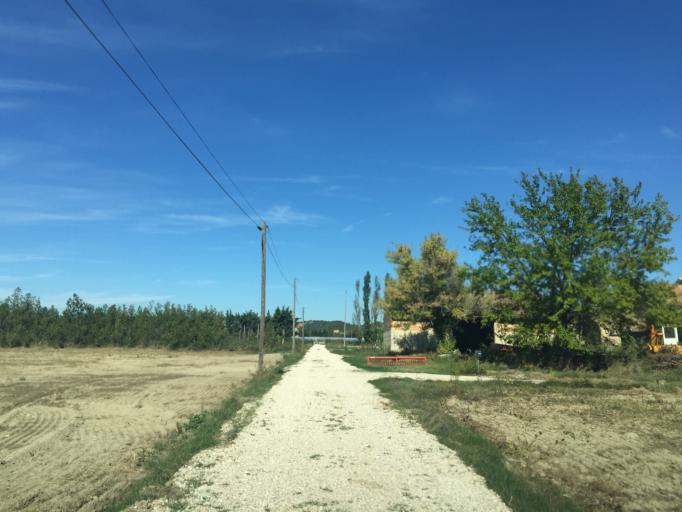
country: FR
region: Provence-Alpes-Cote d'Azur
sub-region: Departement du Vaucluse
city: Piolenc
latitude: 44.1499
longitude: 4.7625
